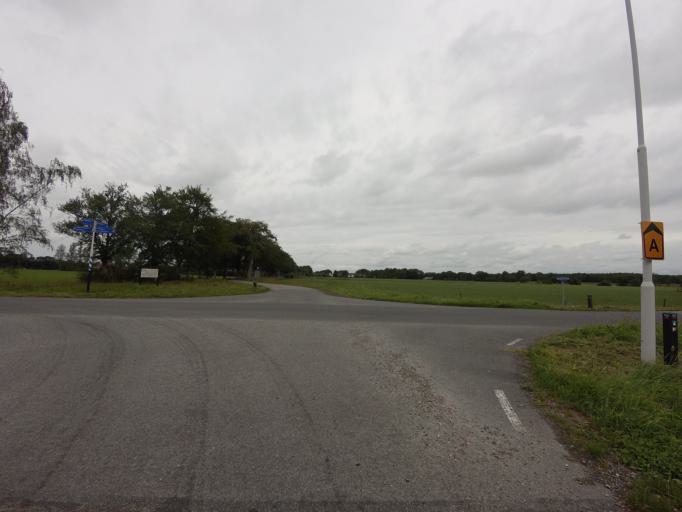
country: NL
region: Friesland
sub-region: Gemeente Weststellingwerf
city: Steggerda
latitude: 52.8816
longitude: 6.0902
